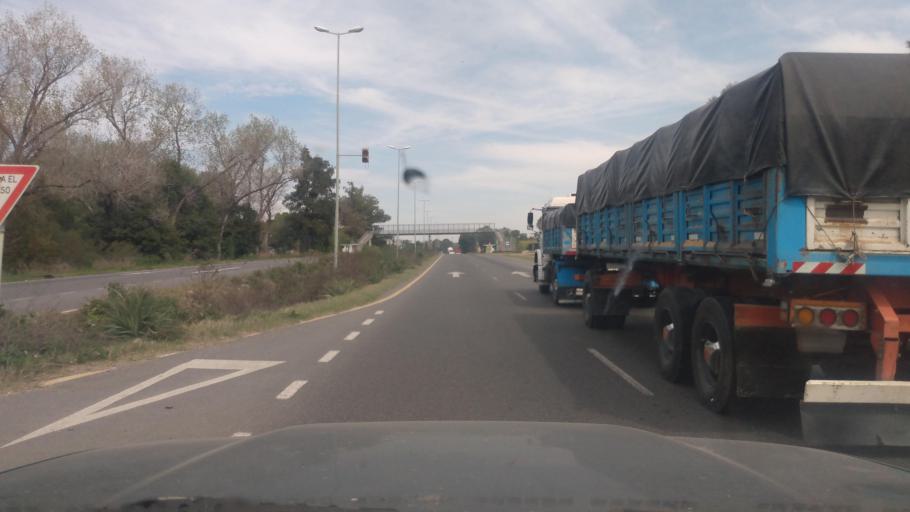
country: AR
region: Buenos Aires
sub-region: Partido de Lujan
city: Lujan
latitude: -34.4453
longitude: -59.0510
